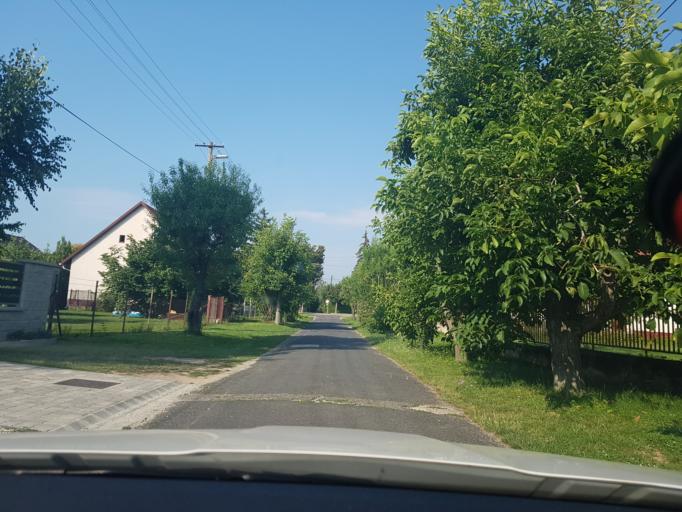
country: HU
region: Veszprem
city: Csopak
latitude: 46.9878
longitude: 17.9791
